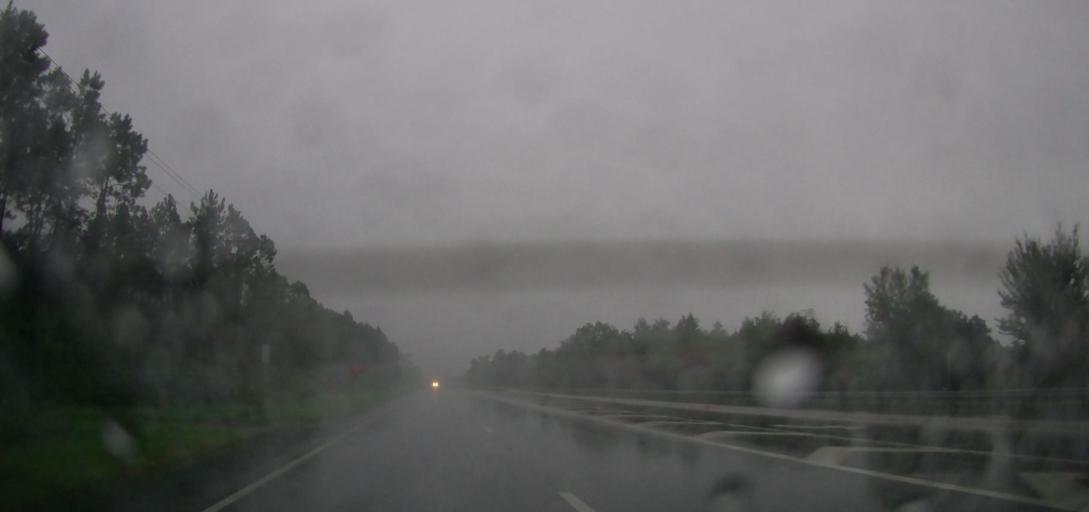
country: US
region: Georgia
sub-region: Clinch County
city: Homerville
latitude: 31.0477
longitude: -82.7173
